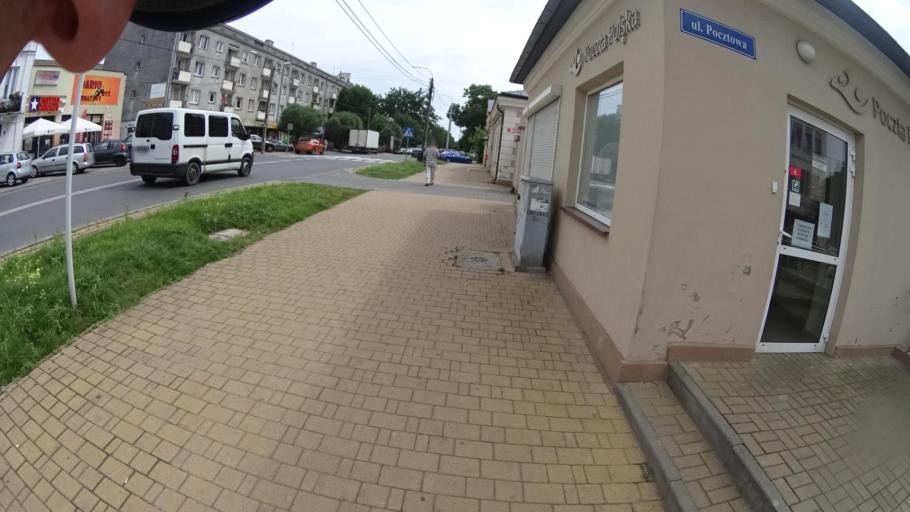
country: PL
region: Masovian Voivodeship
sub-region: Powiat grojecki
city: Grojec
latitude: 51.8648
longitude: 20.8667
